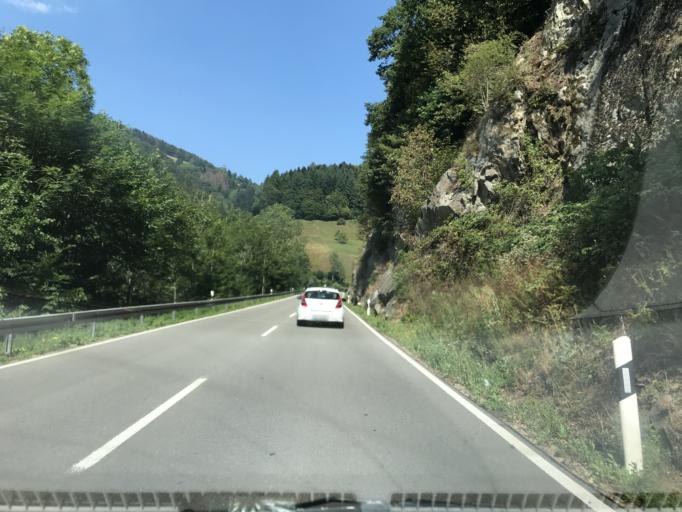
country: DE
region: Baden-Wuerttemberg
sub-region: Freiburg Region
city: Wembach
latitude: 47.7446
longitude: 7.8812
